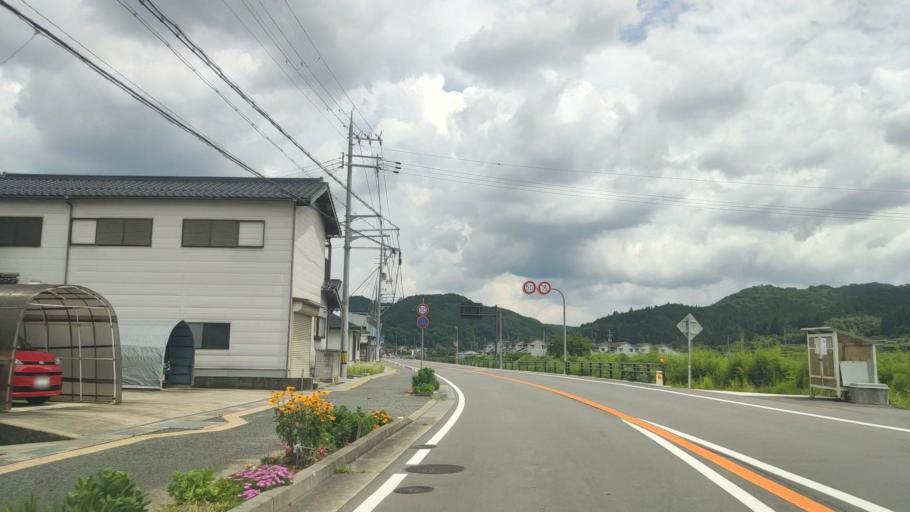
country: JP
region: Hyogo
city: Yamazakicho-nakabirose
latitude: 34.9817
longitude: 134.4396
